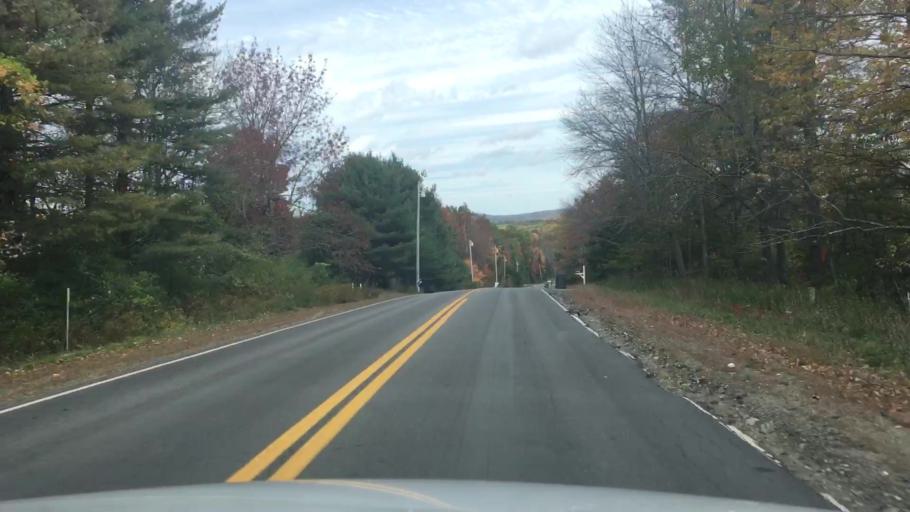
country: US
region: Maine
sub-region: Waldo County
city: Searsmont
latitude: 44.4012
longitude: -69.1369
